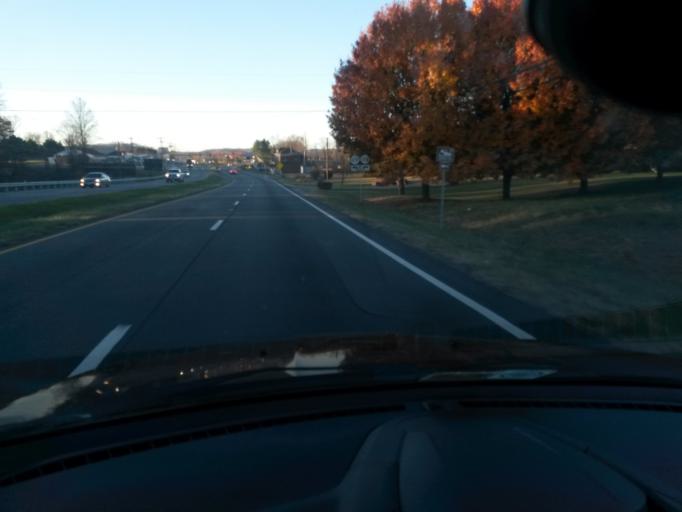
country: US
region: Virginia
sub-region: Franklin County
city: Henry Fork
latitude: 36.9578
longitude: -79.8782
